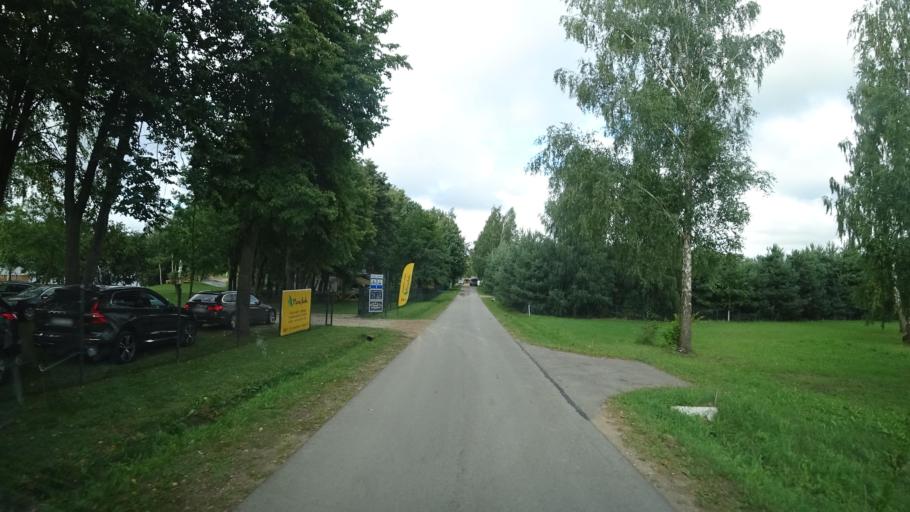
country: LT
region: Marijampoles apskritis
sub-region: Marijampole Municipality
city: Marijampole
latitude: 54.5196
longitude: 23.3393
